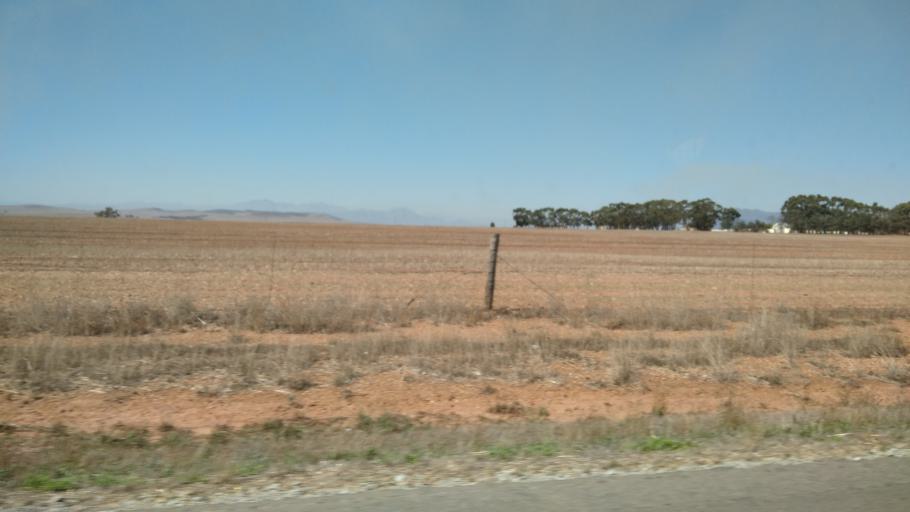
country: ZA
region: Western Cape
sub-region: West Coast District Municipality
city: Moorreesburg
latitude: -33.3202
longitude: 18.6256
